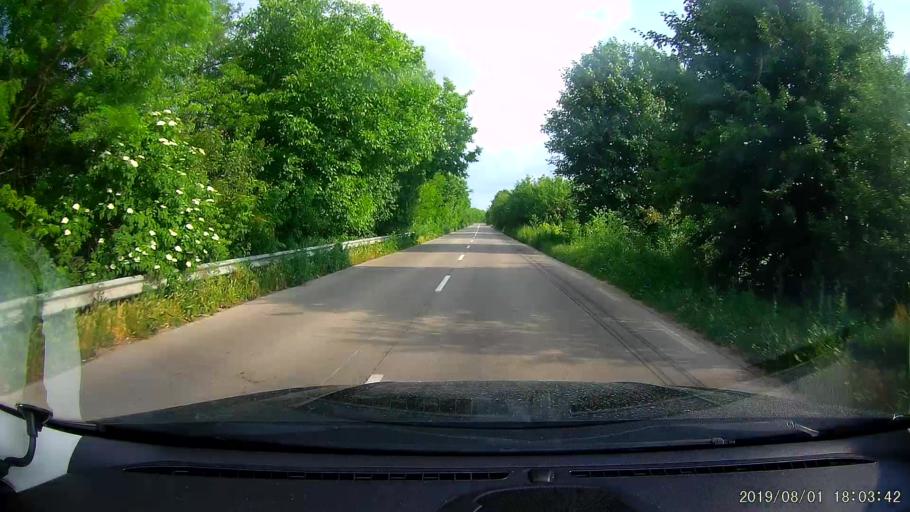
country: BG
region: Silistra
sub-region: Obshtina Alfatar
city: Alfatar
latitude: 43.9214
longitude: 27.2893
